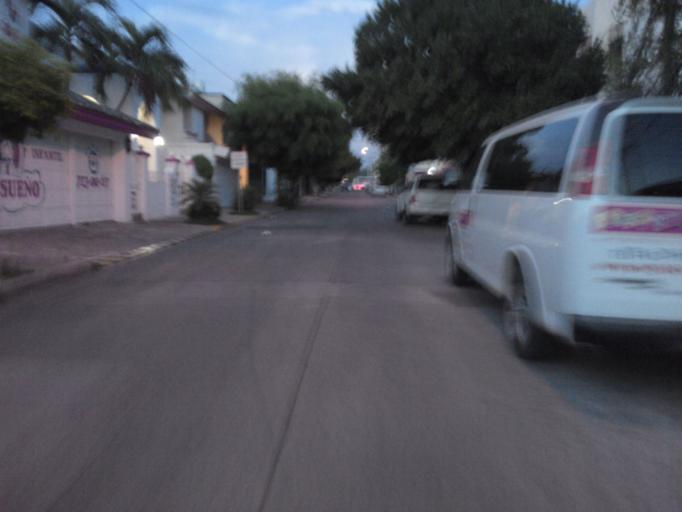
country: MX
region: Sinaloa
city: Culiacan
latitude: 24.7929
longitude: -107.3954
